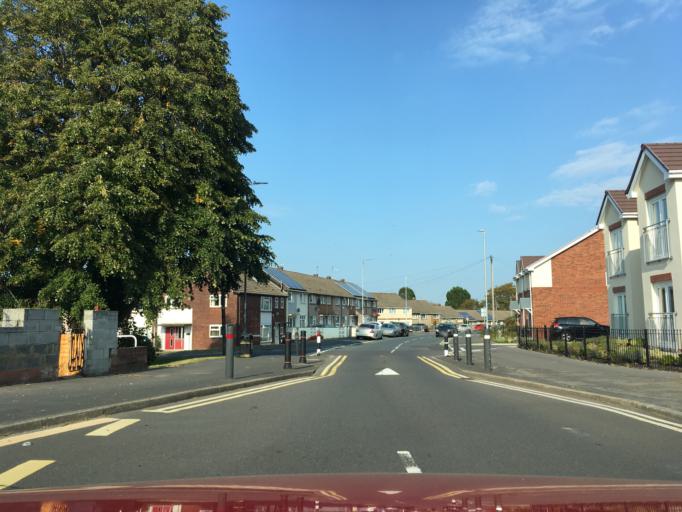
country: GB
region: Wales
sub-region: Newport
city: Newport
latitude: 51.6078
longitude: -3.0293
